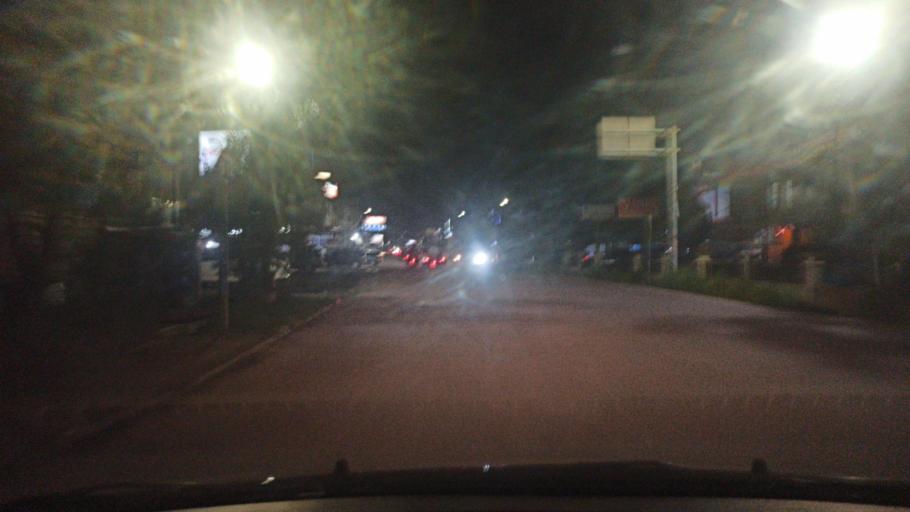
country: ID
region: South Sumatra
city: Plaju
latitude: -2.9507
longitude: 104.7852
